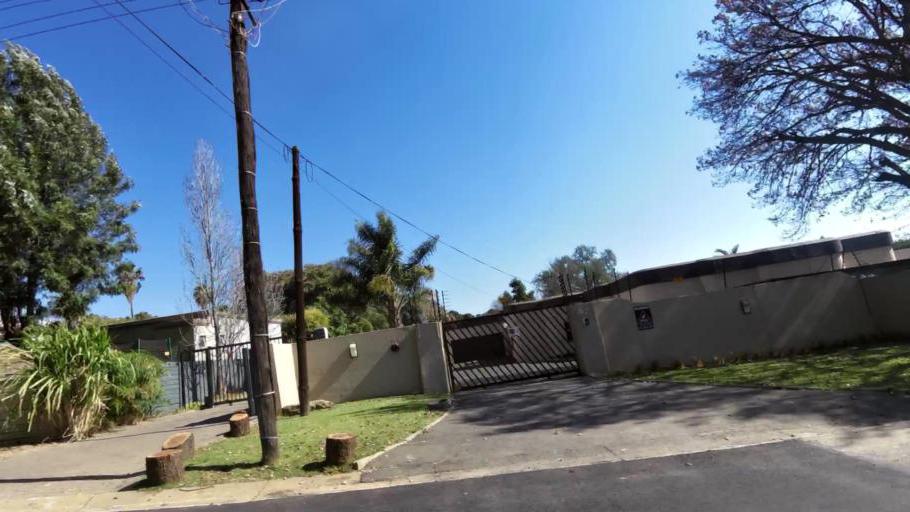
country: ZA
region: Gauteng
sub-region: City of Johannesburg Metropolitan Municipality
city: Roodepoort
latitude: -26.1476
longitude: 27.9440
